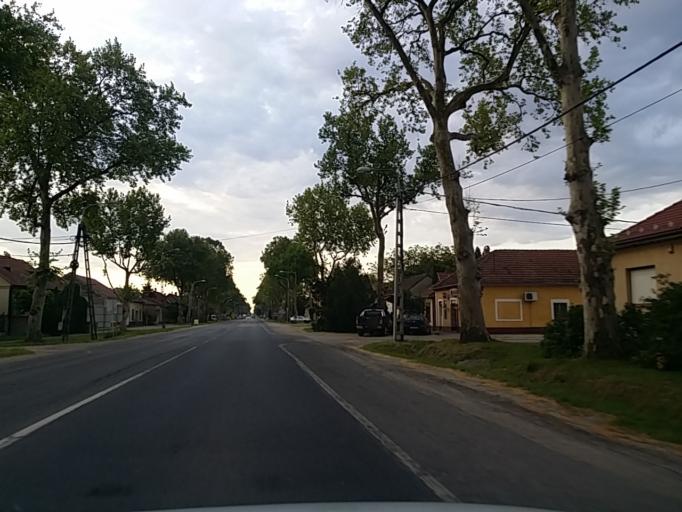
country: HU
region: Bacs-Kiskun
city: Lajosmizse
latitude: 47.0314
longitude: 19.5506
